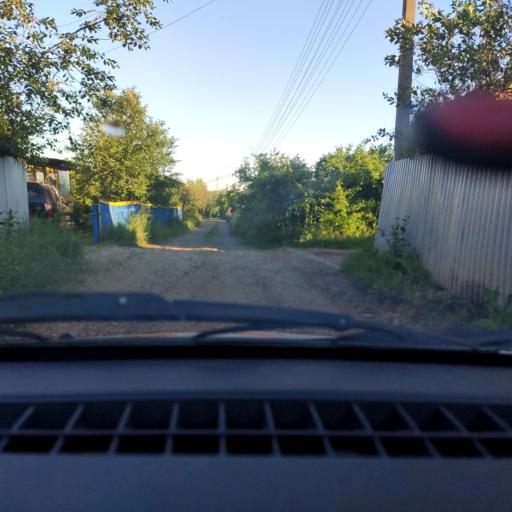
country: RU
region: Bashkortostan
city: Karmaskaly
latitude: 54.3694
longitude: 55.9032
